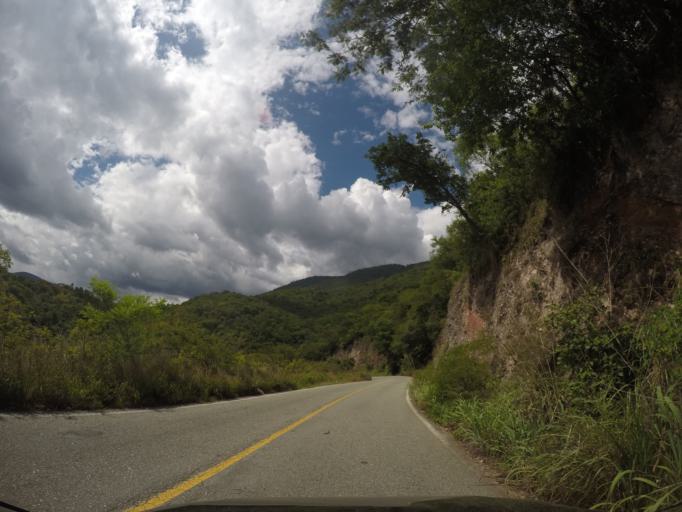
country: MX
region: Oaxaca
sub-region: San Jeronimo Coatlan
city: San Cristobal Honduras
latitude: 16.4344
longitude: -97.0549
